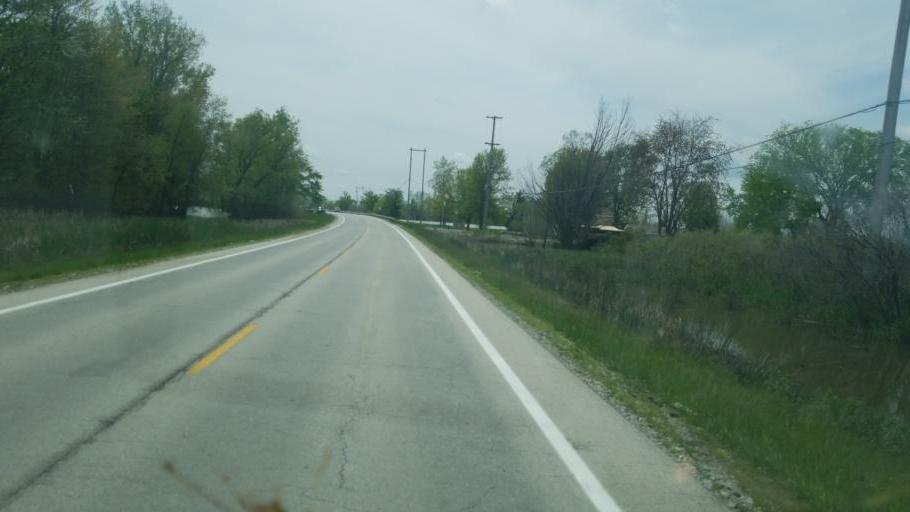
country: US
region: Ohio
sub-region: Ottawa County
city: Oak Harbor
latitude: 41.4542
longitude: -83.0537
